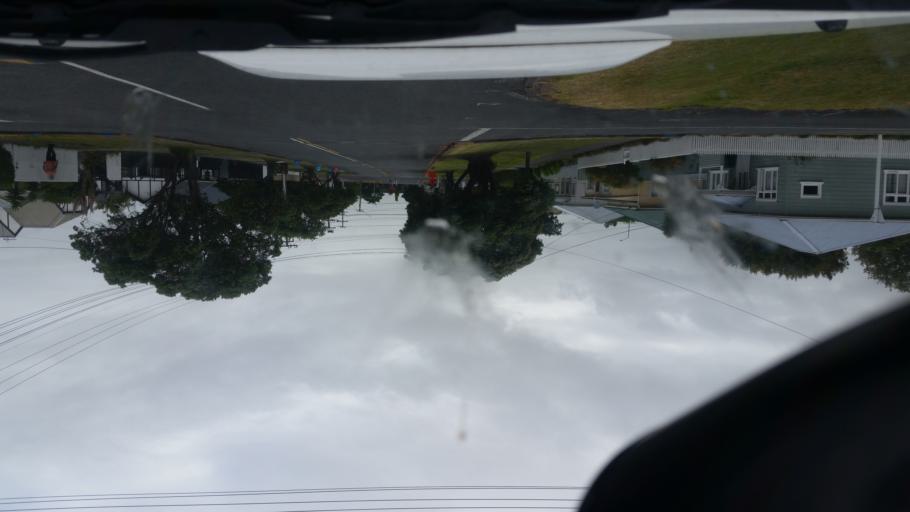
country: NZ
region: Northland
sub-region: Kaipara District
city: Dargaville
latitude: -35.9356
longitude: 173.8736
